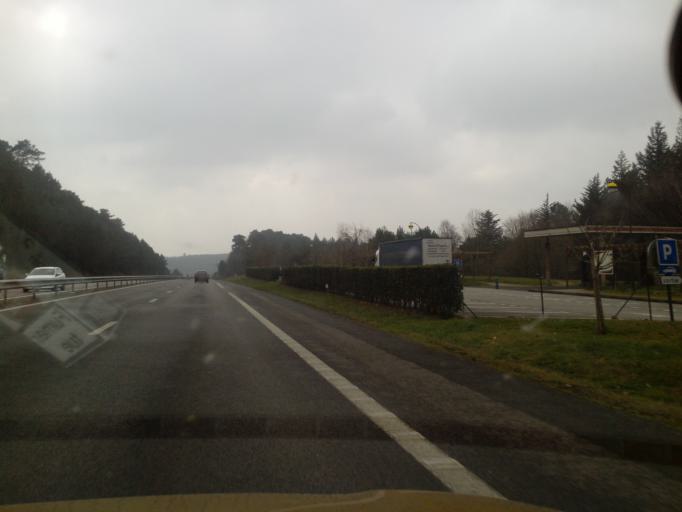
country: FR
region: Brittany
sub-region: Departement du Morbihan
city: Malestroit
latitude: 47.8005
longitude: -2.4468
